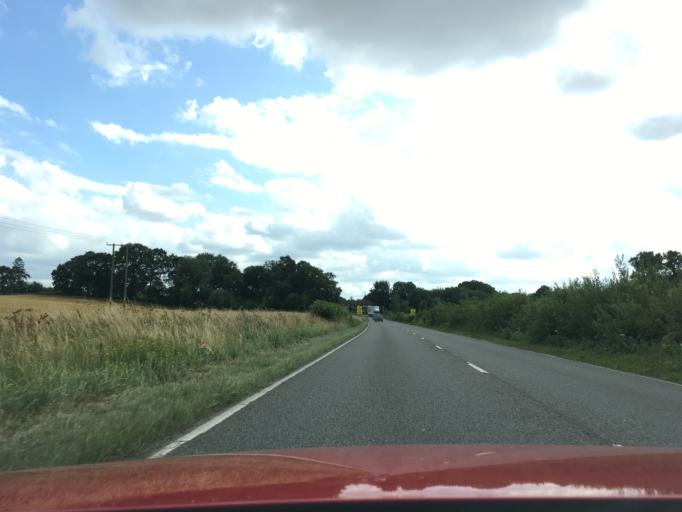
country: GB
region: England
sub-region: Hampshire
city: Kingsclere
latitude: 51.3378
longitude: -1.2586
